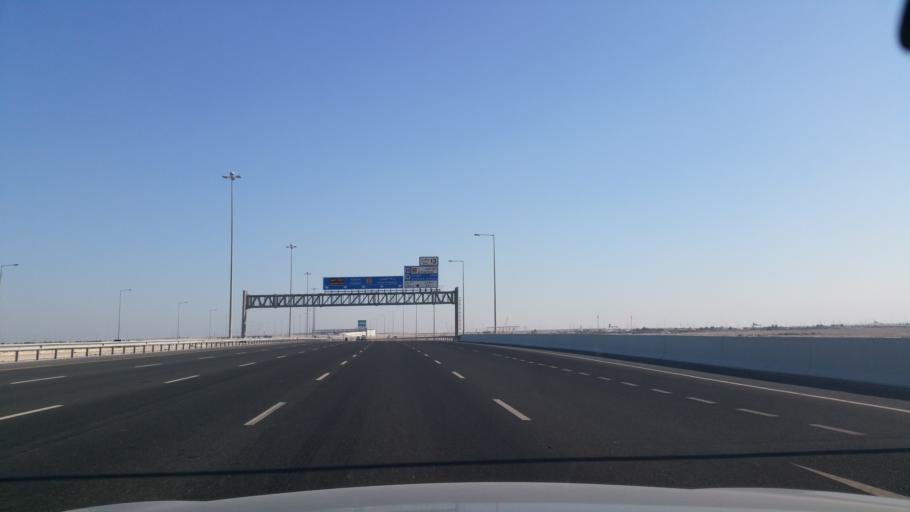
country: QA
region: Al Wakrah
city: Al Wukayr
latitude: 25.1361
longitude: 51.4775
